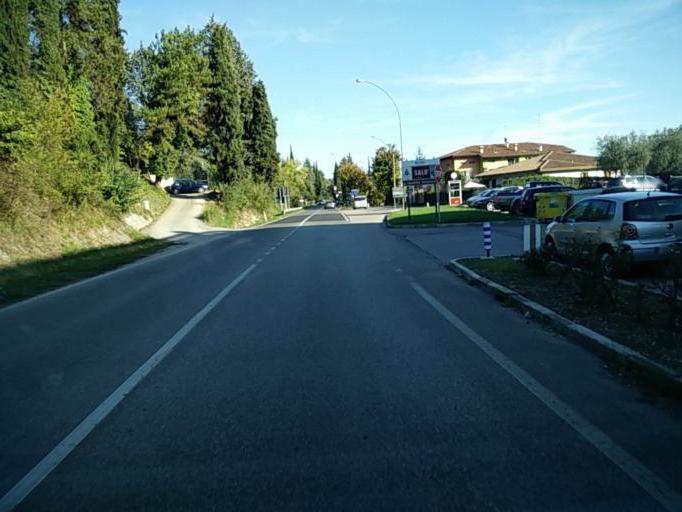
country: IT
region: Lombardy
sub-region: Provincia di Brescia
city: Salo
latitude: 45.6119
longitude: 10.5115
